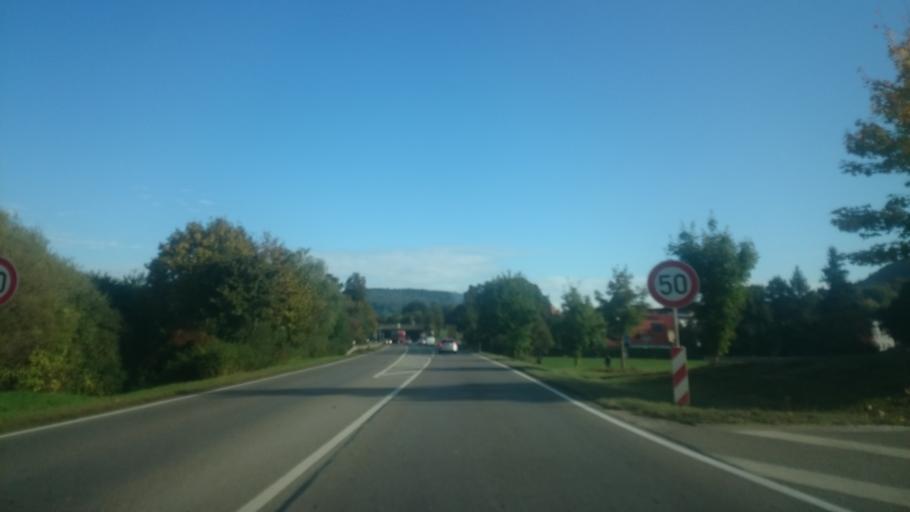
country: DE
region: Bavaria
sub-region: Regierungsbezirk Mittelfranken
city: Weissenburg in Bayern
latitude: 49.0242
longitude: 10.9832
